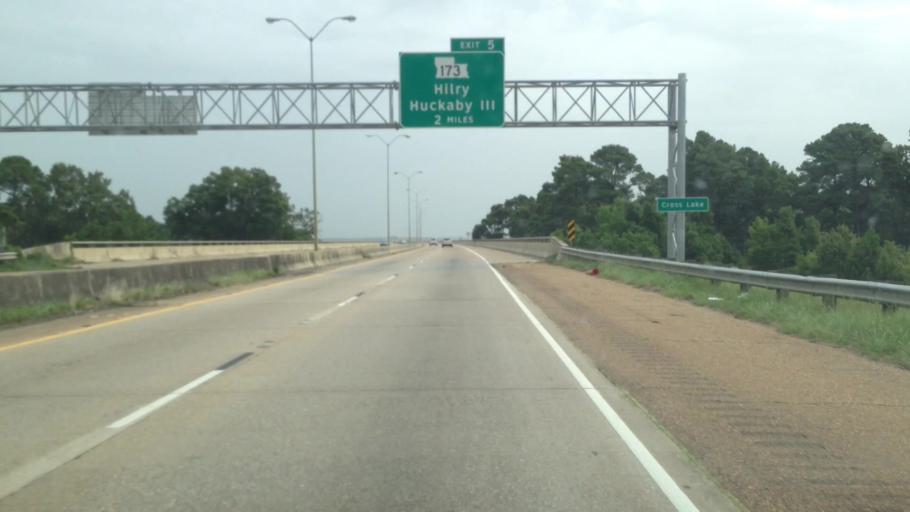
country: US
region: Louisiana
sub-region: Caddo Parish
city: Shreveport
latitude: 32.4942
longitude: -93.8219
